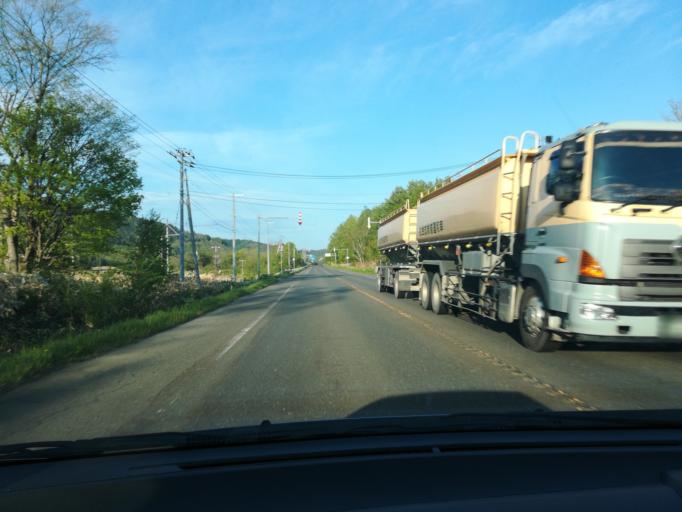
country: JP
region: Hokkaido
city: Shimo-furano
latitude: 43.1392
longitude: 142.6145
